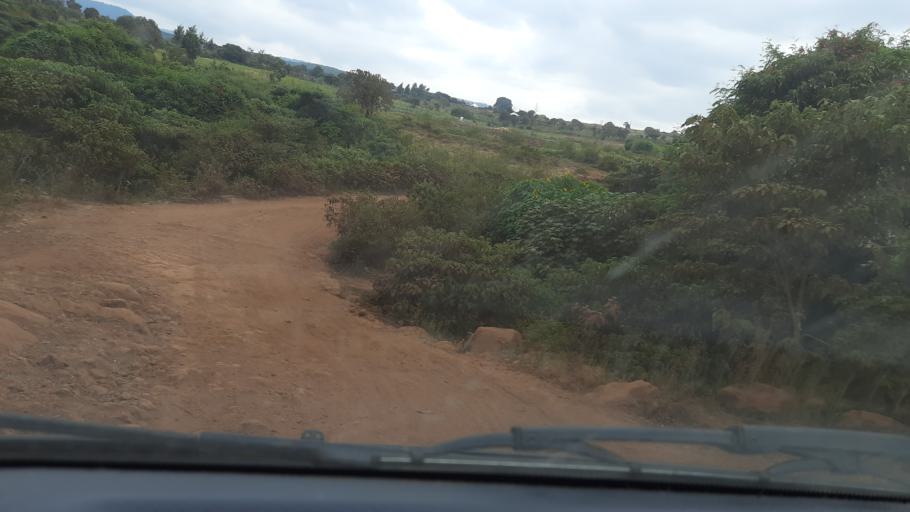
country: TZ
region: Arusha
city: Kingori
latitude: -2.8441
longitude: 37.2240
